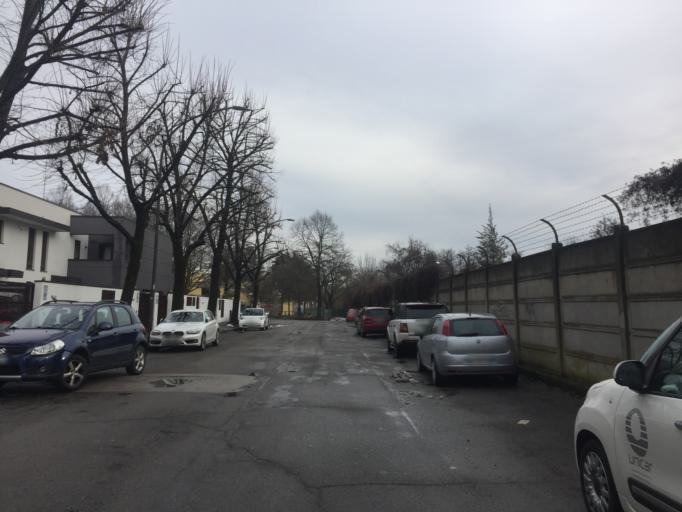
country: IT
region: Emilia-Romagna
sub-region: Provincia di Bologna
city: Bologna
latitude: 44.5098
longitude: 11.3045
